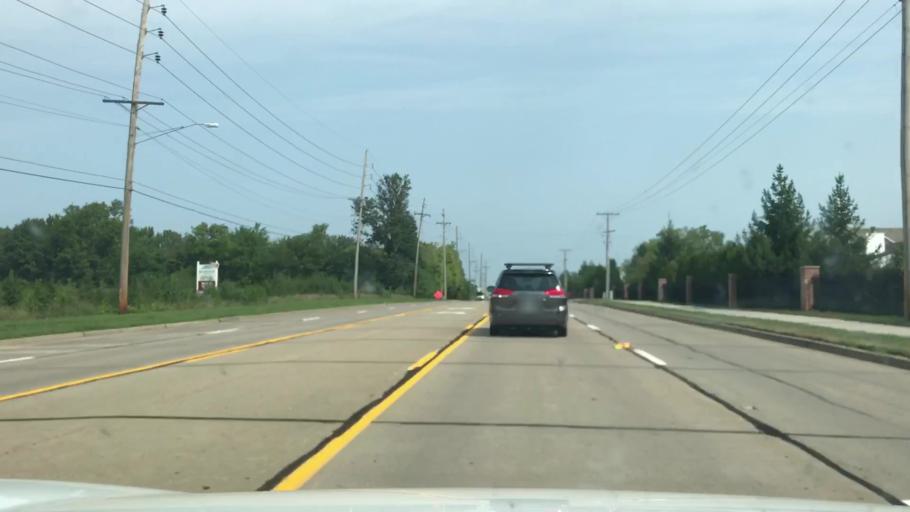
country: US
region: Missouri
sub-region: Saint Charles County
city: Dardenne Prairie
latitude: 38.7773
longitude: -90.7374
